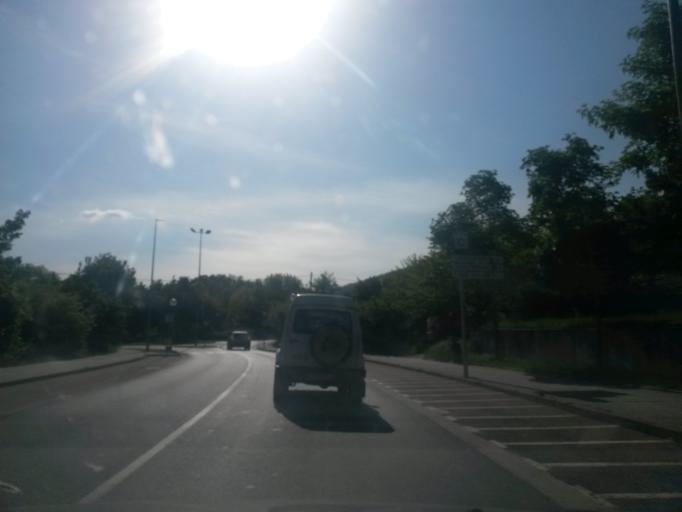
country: ES
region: Catalonia
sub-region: Provincia de Girona
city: Olot
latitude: 42.1674
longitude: 2.4808
